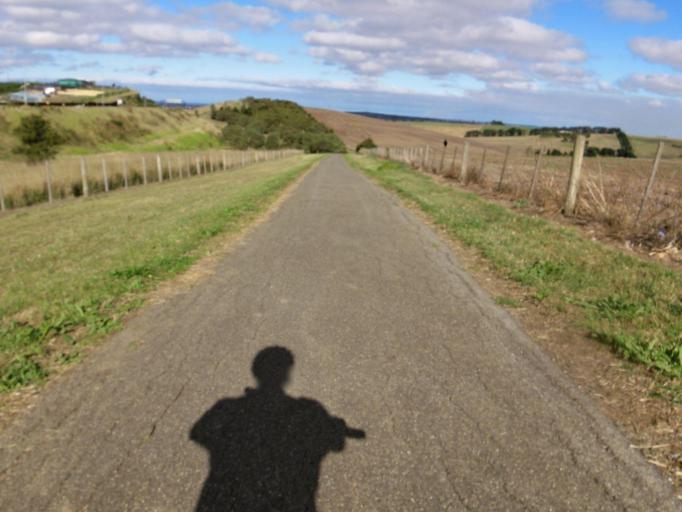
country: AU
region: Victoria
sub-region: Greater Geelong
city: Wandana Heights
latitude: -38.1733
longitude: 144.2913
